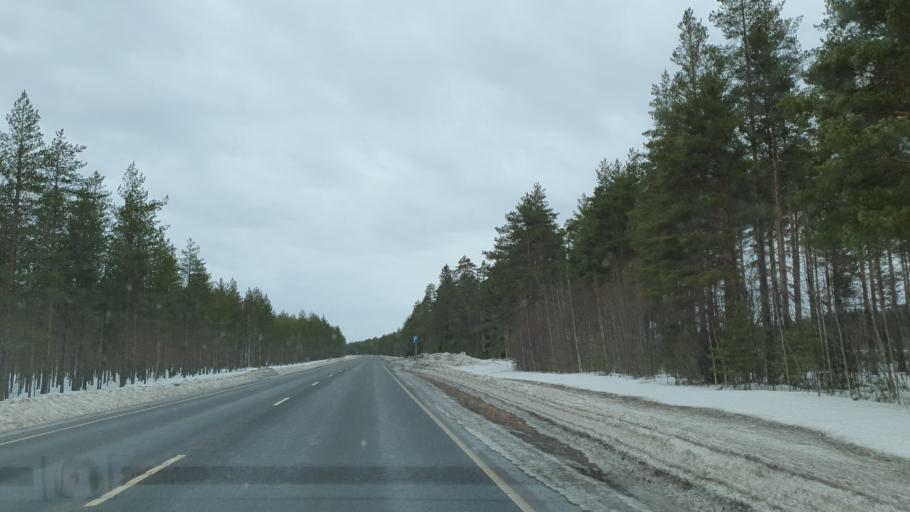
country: FI
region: Northern Ostrobothnia
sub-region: Oulunkaari
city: Utajaervi
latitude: 64.7282
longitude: 26.4865
